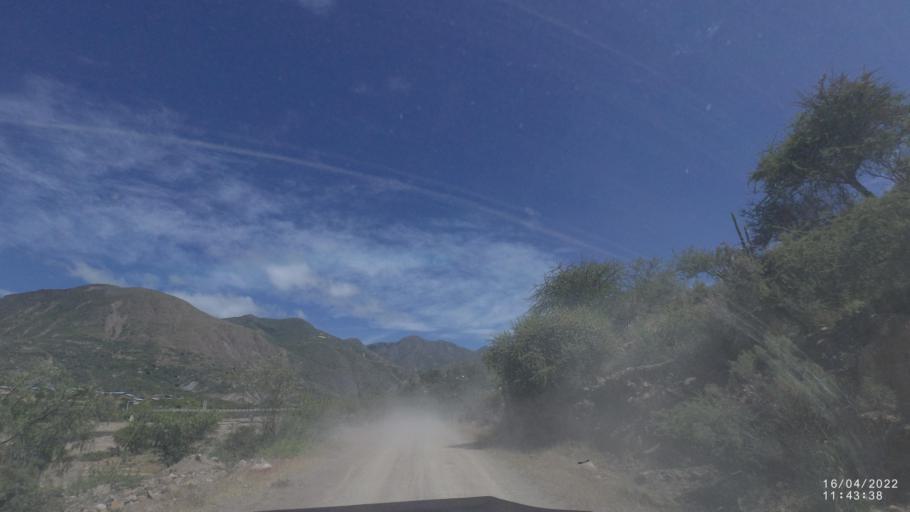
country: BO
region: Cochabamba
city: Mizque
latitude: -17.9819
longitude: -65.6297
